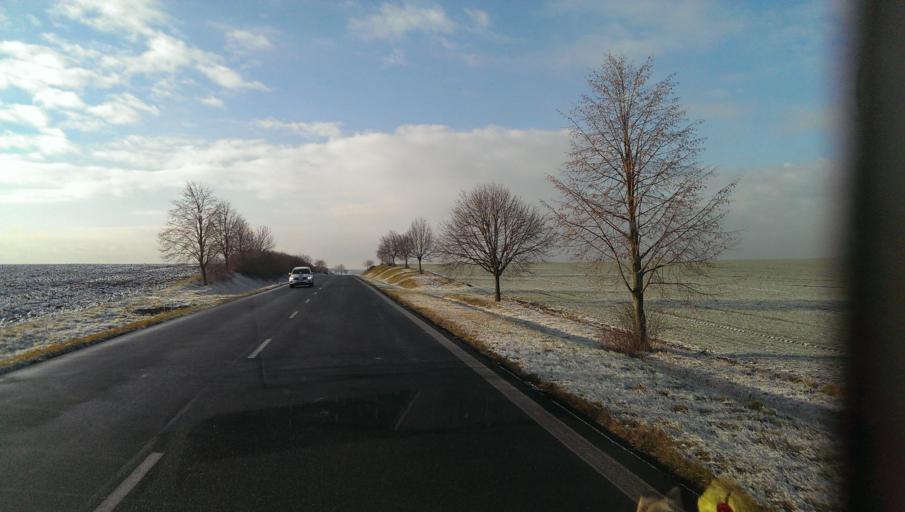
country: CZ
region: Ustecky
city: Budyne nad Ohri
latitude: 50.4086
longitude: 14.1678
